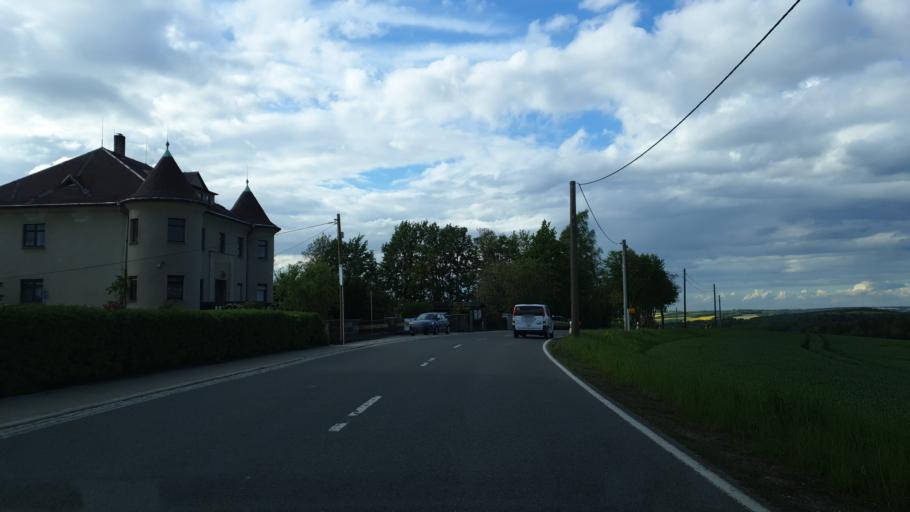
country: DE
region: Saxony
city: Lichtenstein
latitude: 50.7311
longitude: 12.6372
